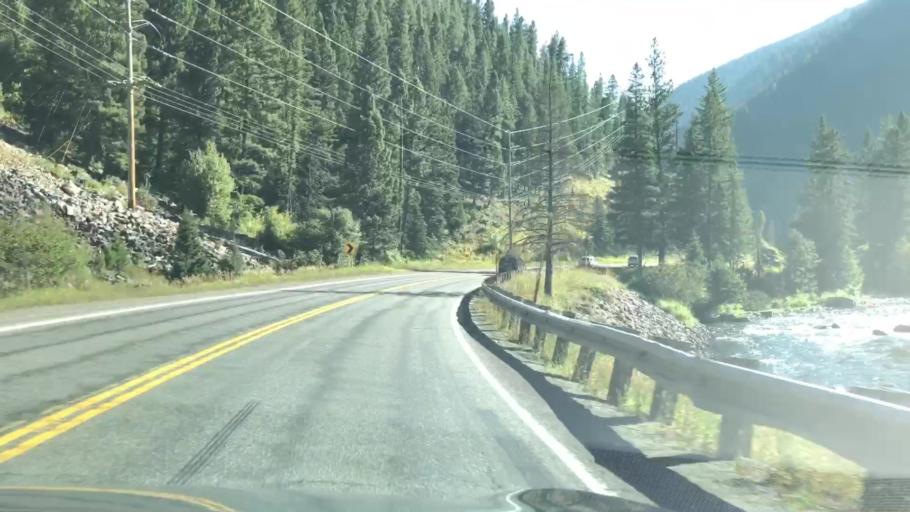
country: US
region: Montana
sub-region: Gallatin County
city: Big Sky
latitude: 45.3777
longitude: -111.1737
